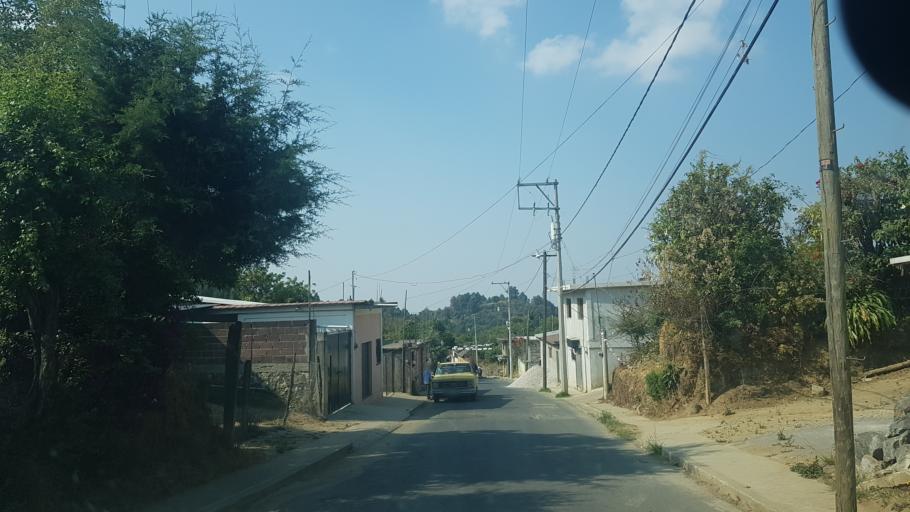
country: MX
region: Morelos
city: Hueyapan
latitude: 18.8896
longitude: -98.6804
